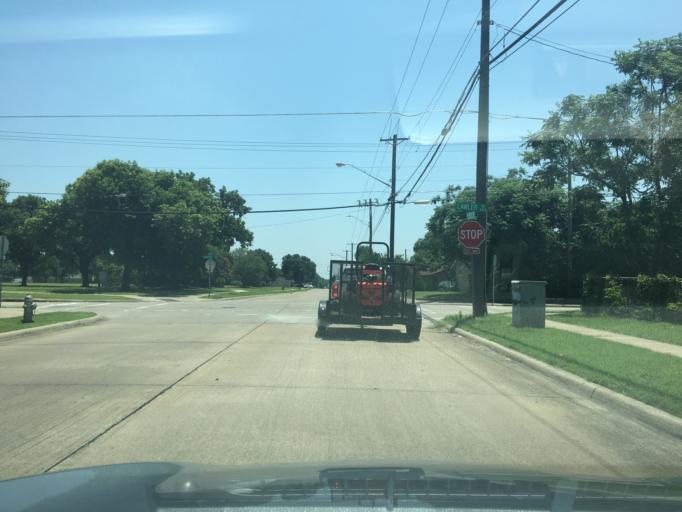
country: US
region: Texas
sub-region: Dallas County
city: Richardson
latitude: 32.9243
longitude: -96.6926
